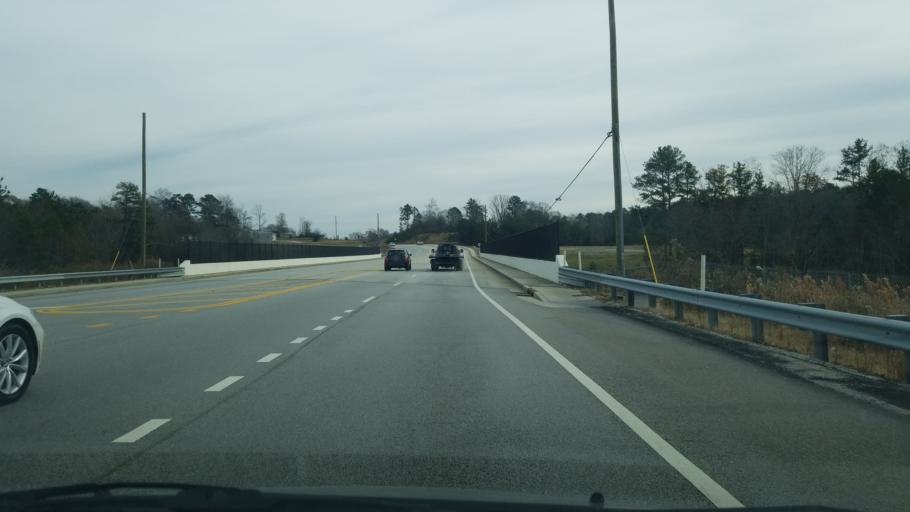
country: US
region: Tennessee
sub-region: Hamilton County
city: Harrison
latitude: 35.0720
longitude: -85.1079
